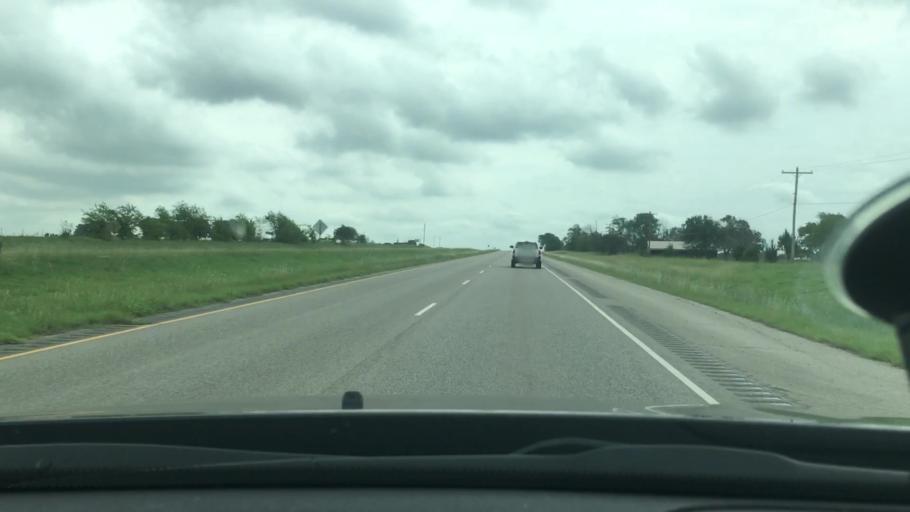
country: US
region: Oklahoma
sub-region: Carter County
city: Wilson
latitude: 34.1729
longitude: -97.4678
